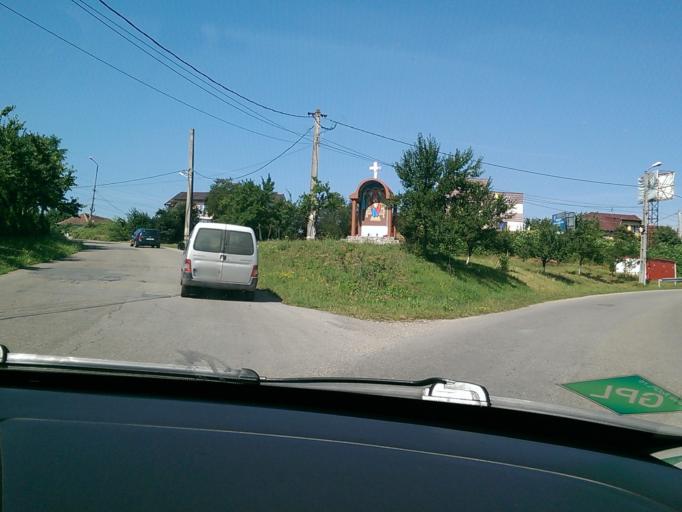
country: RO
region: Bihor
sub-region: Comuna Sanmartin
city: Sanmartin
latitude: 47.0013
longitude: 21.9822
